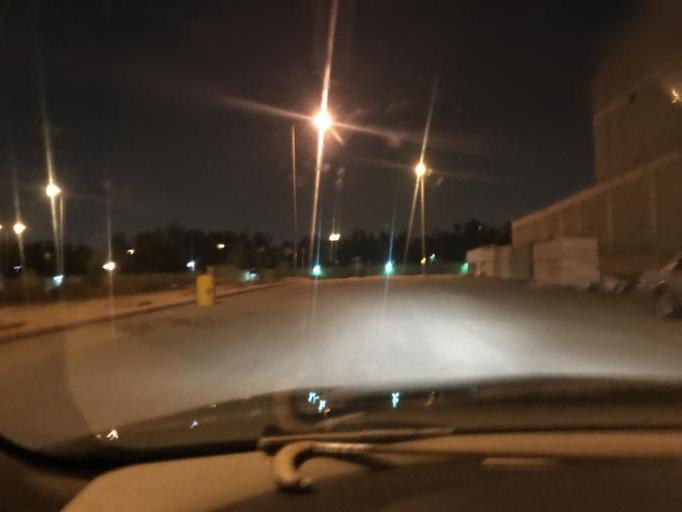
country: SA
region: Ar Riyad
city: Riyadh
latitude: 24.8162
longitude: 46.7169
